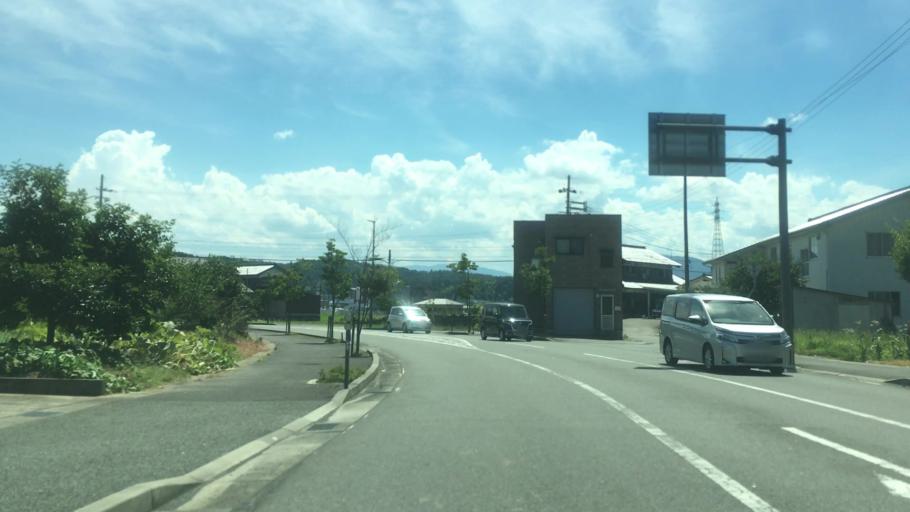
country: JP
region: Hyogo
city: Toyooka
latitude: 35.5582
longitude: 134.8161
